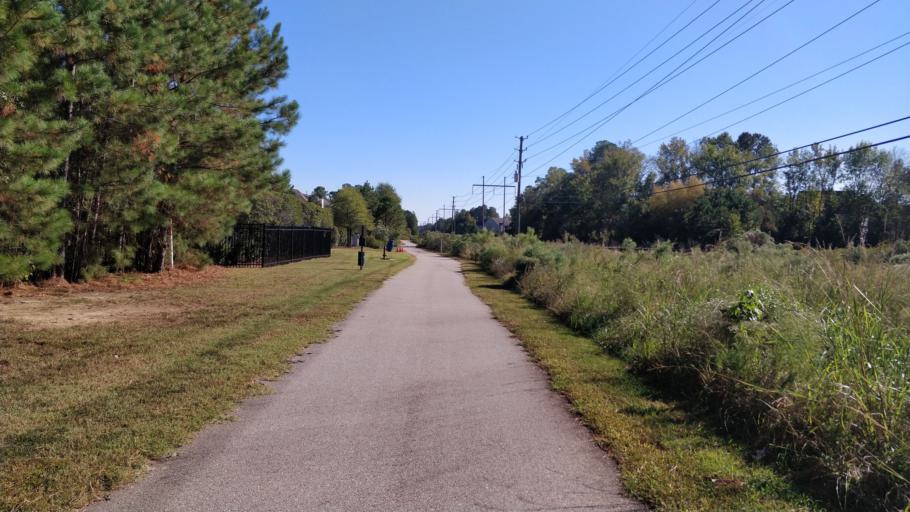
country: US
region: North Carolina
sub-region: Wake County
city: Morrisville
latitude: 35.8387
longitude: -78.8440
